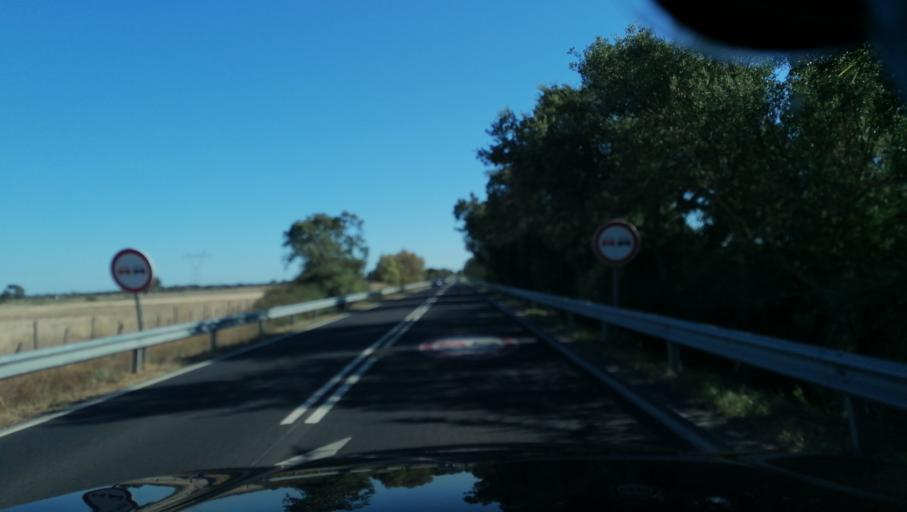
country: PT
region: Santarem
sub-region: Benavente
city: Samora Correia
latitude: 38.8719
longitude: -8.8812
